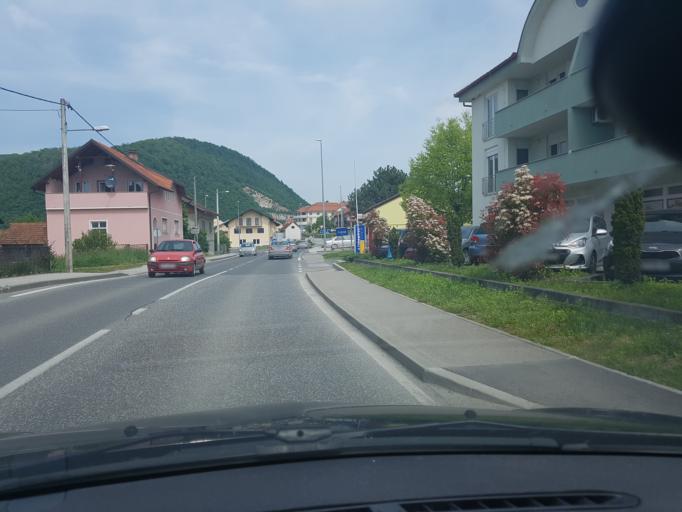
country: HR
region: Krapinsko-Zagorska
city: Pregrada
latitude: 46.1588
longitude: 15.7550
